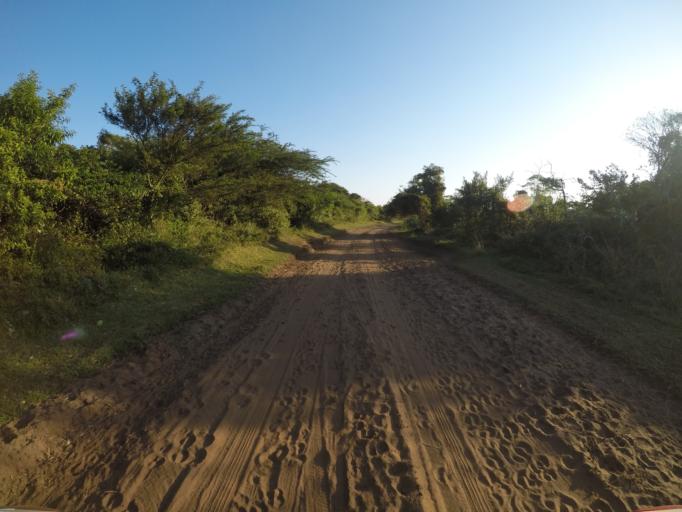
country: ZA
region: KwaZulu-Natal
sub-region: uThungulu District Municipality
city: KwaMbonambi
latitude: -28.6910
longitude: 32.2037
